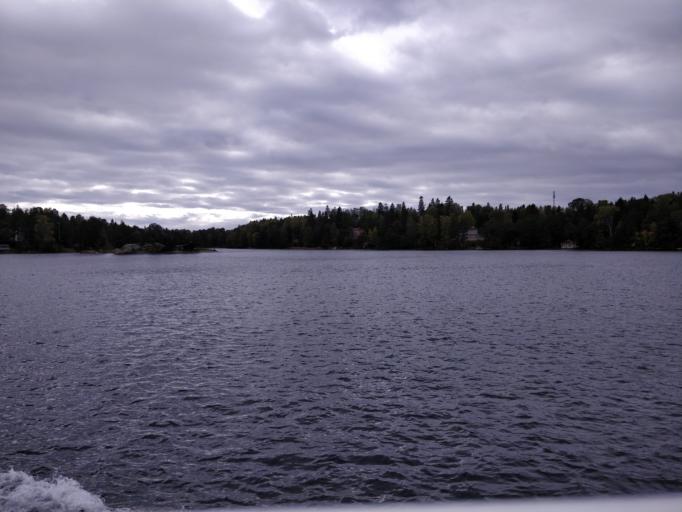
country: FI
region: Uusimaa
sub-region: Helsinki
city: Vantaa
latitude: 60.1718
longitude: 25.0912
